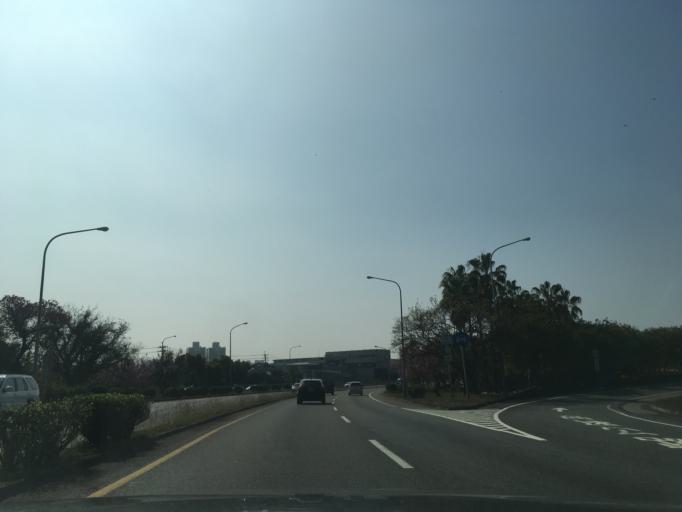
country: TW
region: Taiwan
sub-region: Taichung City
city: Taichung
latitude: 24.2050
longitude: 120.6568
